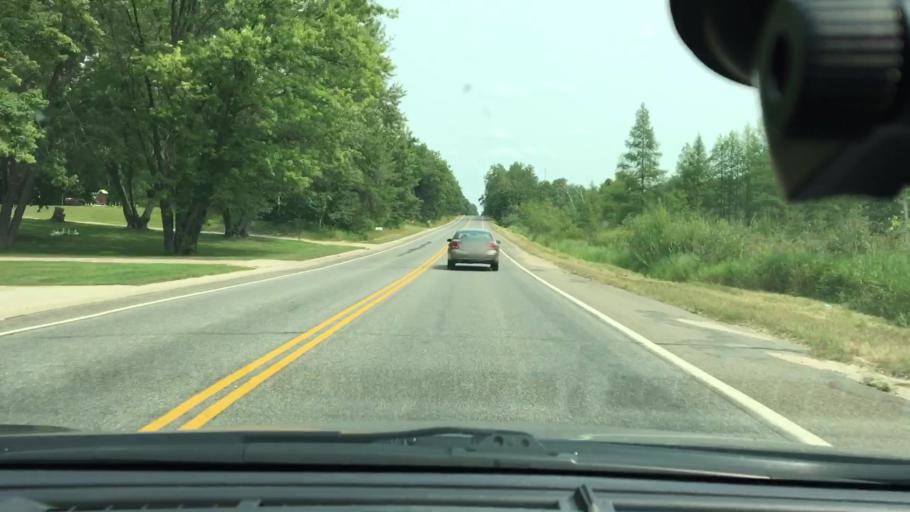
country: US
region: Minnesota
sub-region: Cass County
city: East Gull Lake
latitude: 46.4128
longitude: -94.3195
